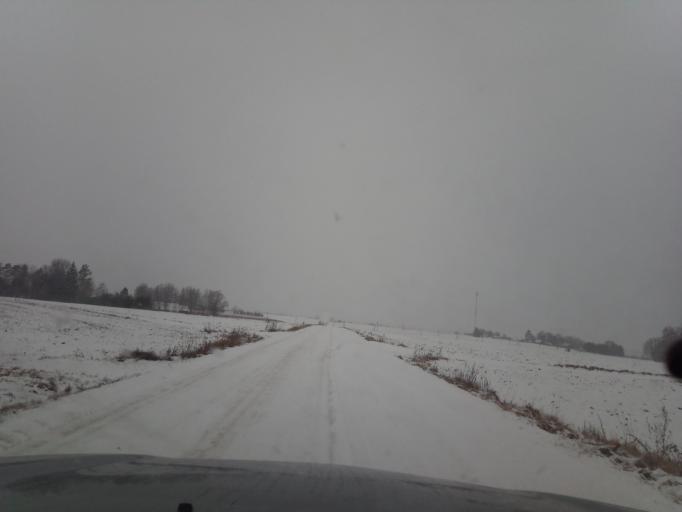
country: LT
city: Ramygala
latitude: 55.5638
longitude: 24.3460
